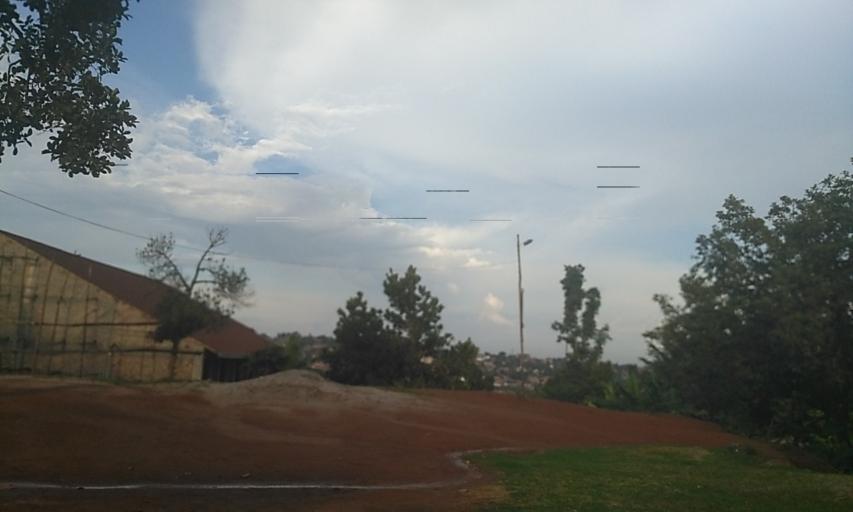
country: UG
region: Central Region
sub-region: Wakiso District
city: Kajansi
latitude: 0.2579
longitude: 32.5322
